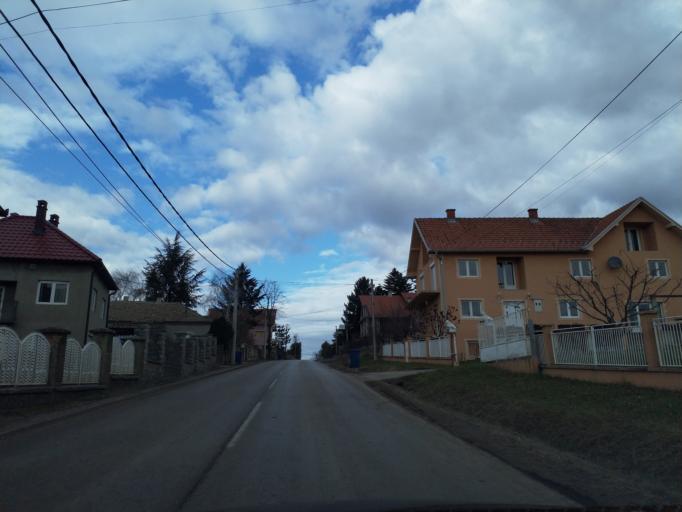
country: RS
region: Central Serbia
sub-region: Belgrade
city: Grocka
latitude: 44.6033
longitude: 20.7258
